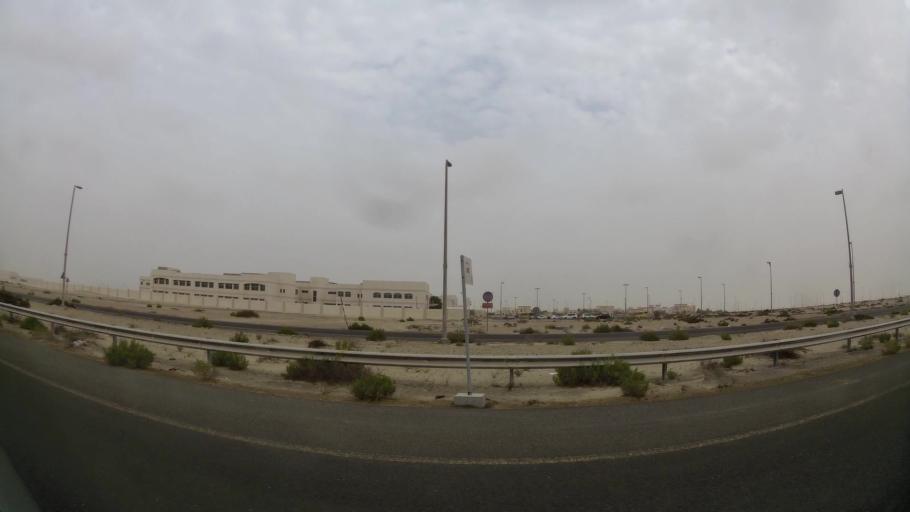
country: AE
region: Abu Dhabi
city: Abu Dhabi
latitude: 24.3904
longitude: 54.7364
